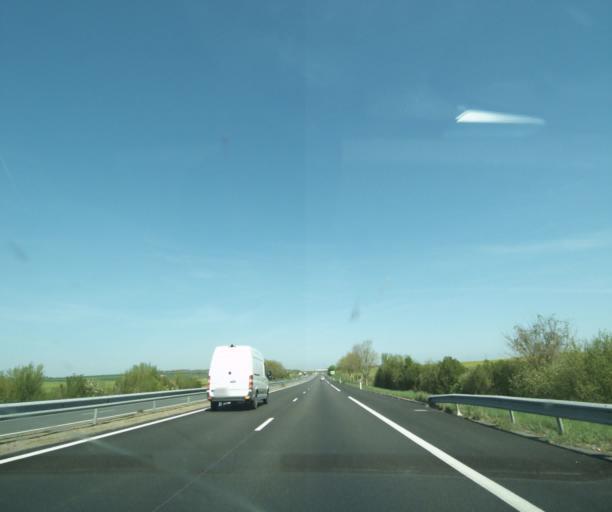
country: FR
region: Bourgogne
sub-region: Departement de la Nievre
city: La Charite-sur-Loire
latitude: 47.1428
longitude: 3.0450
